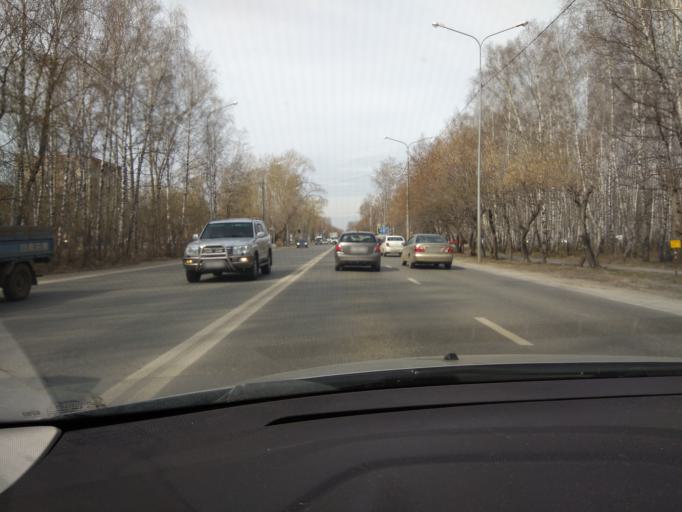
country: RU
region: Tjumen
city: Melioratorov
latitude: 57.1788
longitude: 65.5934
